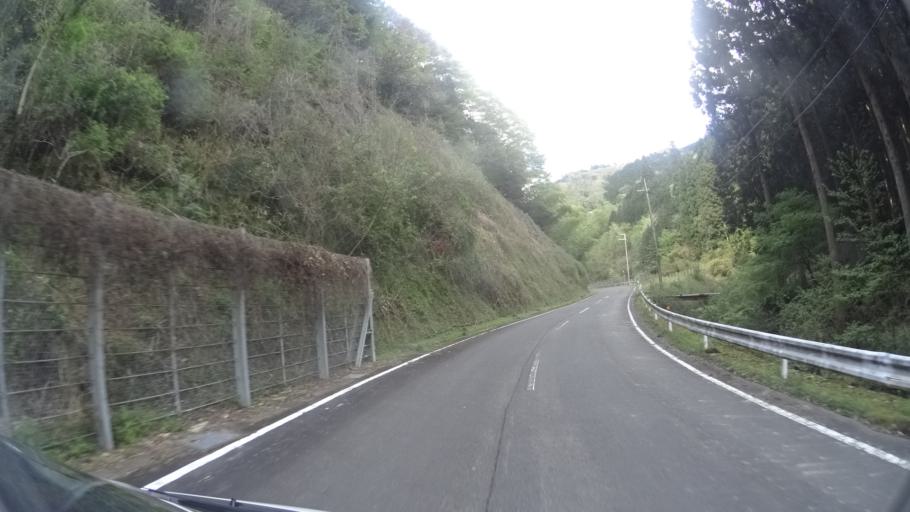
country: JP
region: Kyoto
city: Ayabe
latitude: 35.2530
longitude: 135.3105
